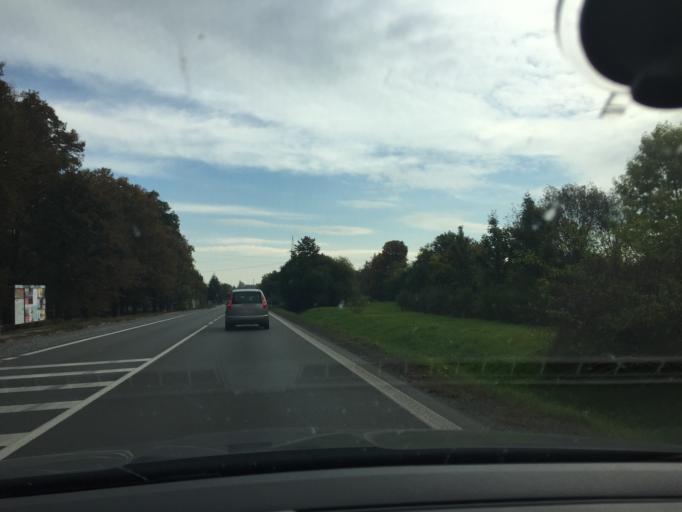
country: CZ
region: Praha
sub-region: Praha 14
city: Hostavice
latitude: 50.0907
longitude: 14.5414
